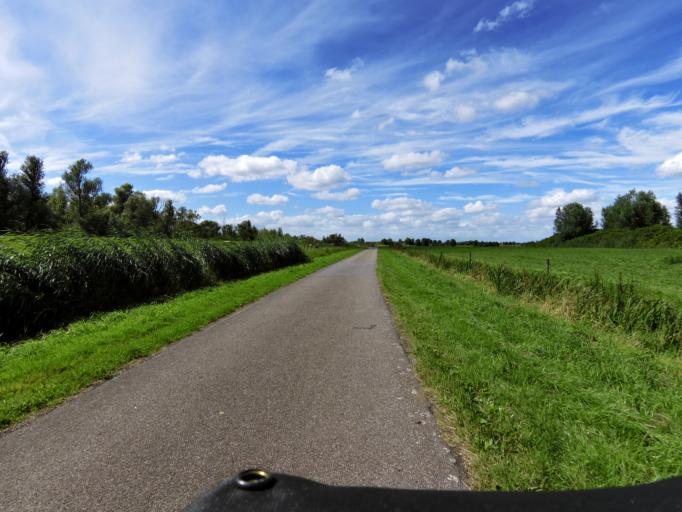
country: NL
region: South Holland
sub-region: Gemeente Zwijndrecht
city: Heerjansdam
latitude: 51.8151
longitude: 4.5698
